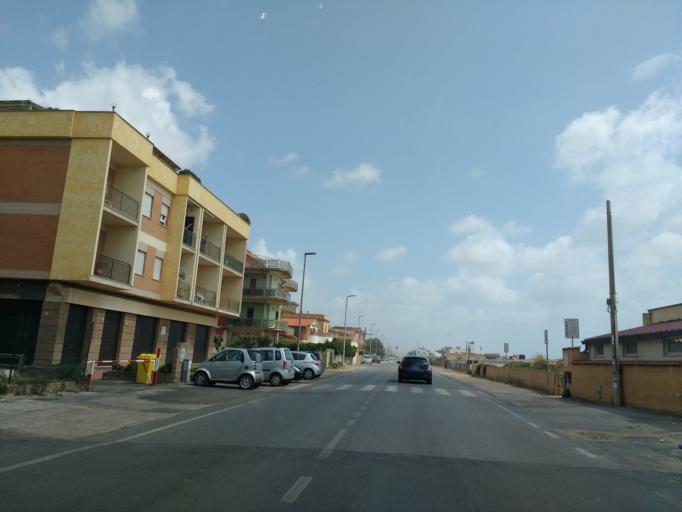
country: IT
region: Latium
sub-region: Citta metropolitana di Roma Capitale
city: Torvaianica Alta
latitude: 41.6094
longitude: 12.4749
